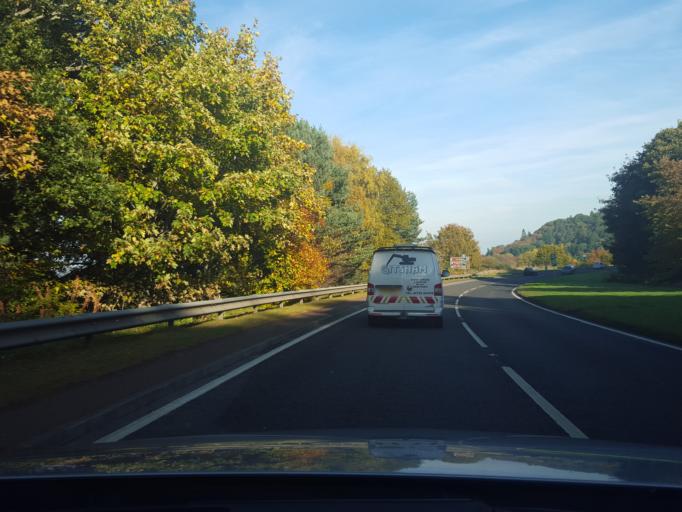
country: GB
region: Scotland
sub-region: Highland
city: Inverness
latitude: 57.4619
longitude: -4.2564
